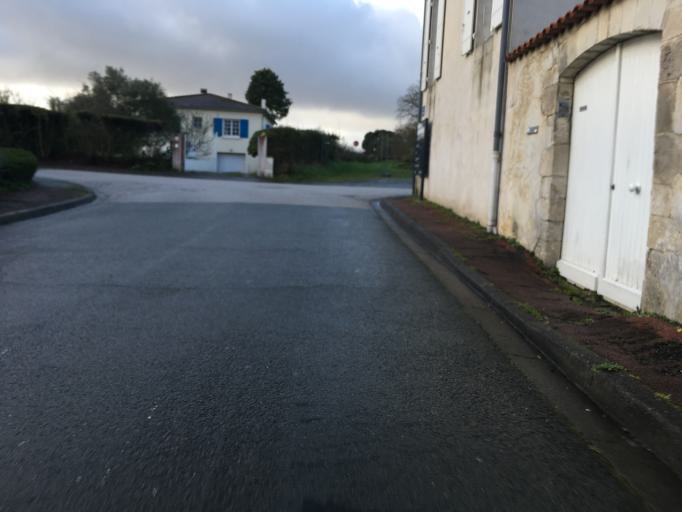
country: FR
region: Poitou-Charentes
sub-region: Departement de la Charente-Maritime
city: Nieul-sur-Mer
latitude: 46.1915
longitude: -1.1854
